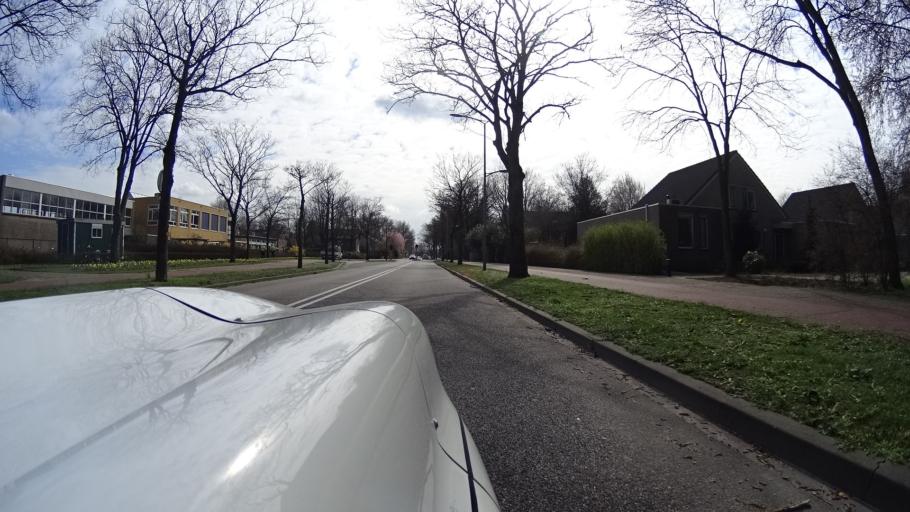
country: NL
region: North Brabant
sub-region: Gemeente 's-Hertogenbosch
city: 's-Hertogenbosch
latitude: 51.7076
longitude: 5.3617
